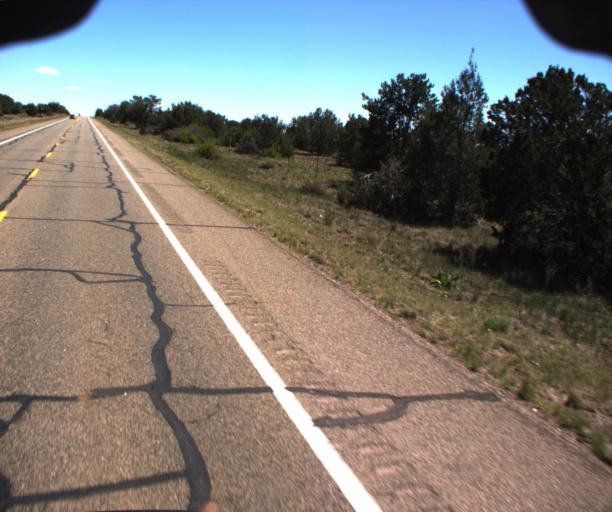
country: US
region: Arizona
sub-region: Coconino County
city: Williams
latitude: 35.1779
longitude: -112.4641
